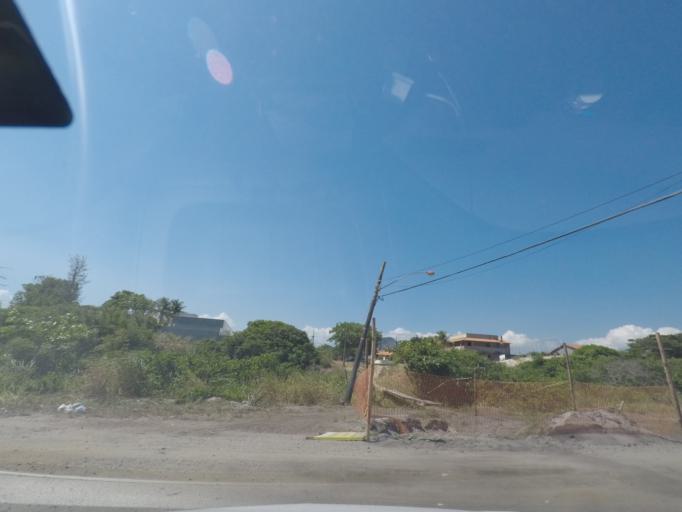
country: BR
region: Rio de Janeiro
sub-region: Marica
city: Marica
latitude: -22.9717
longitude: -42.9154
